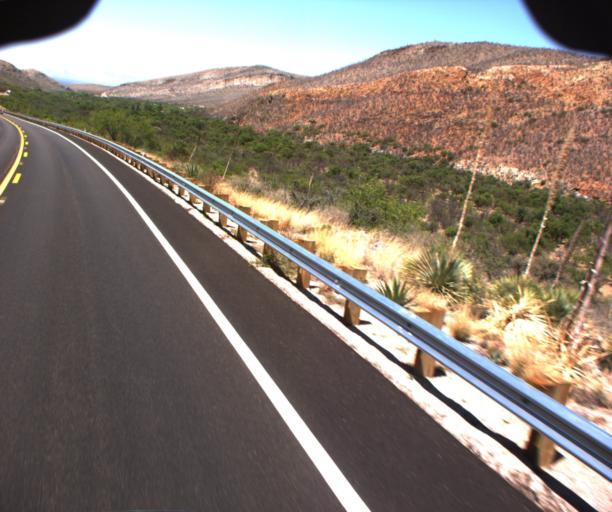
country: US
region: Arizona
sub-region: Cochise County
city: Bisbee
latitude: 31.5060
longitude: -110.0091
